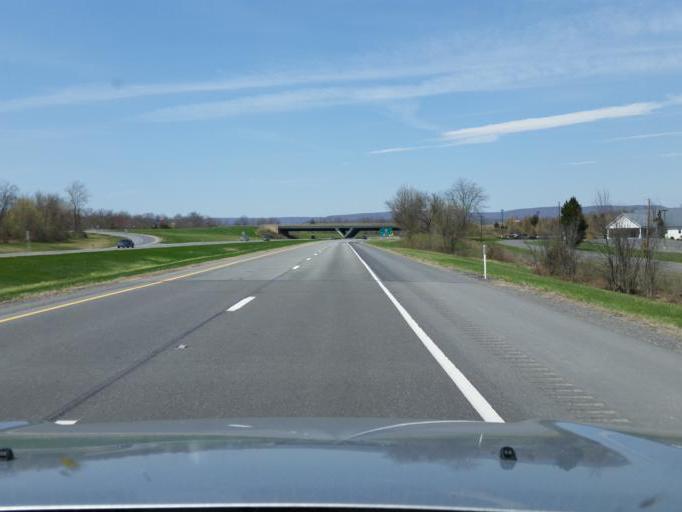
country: US
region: Pennsylvania
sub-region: Juniata County
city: Mifflintown
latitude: 40.5524
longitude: -77.3582
